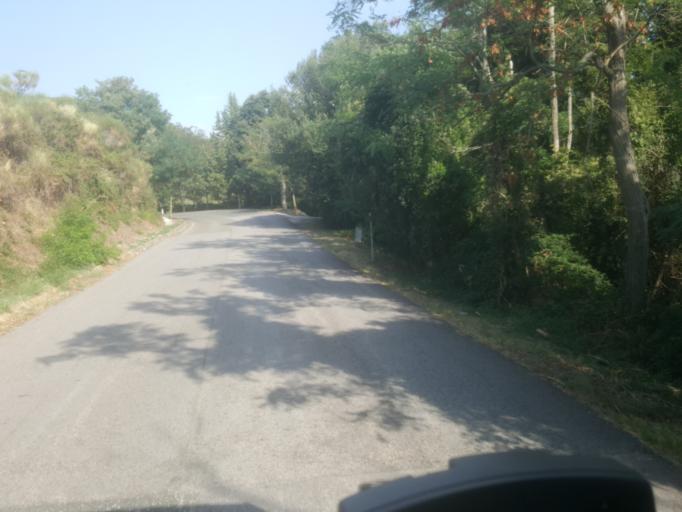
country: IT
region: Tuscany
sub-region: Province of Florence
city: Montaione
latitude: 43.4875
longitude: 10.9013
